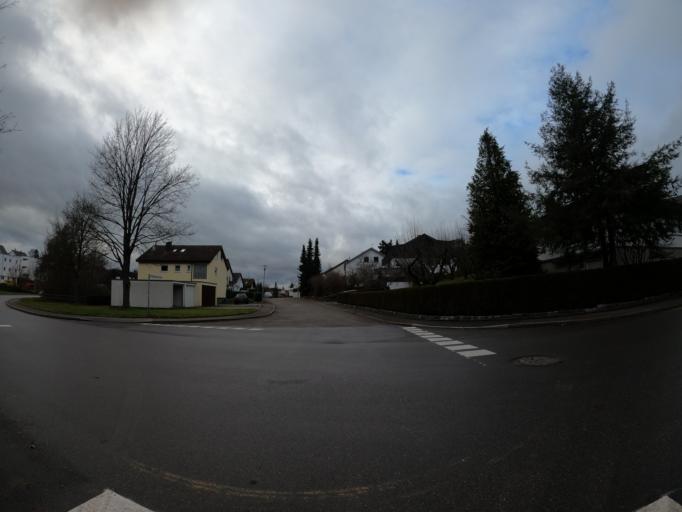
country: DE
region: Baden-Wuerttemberg
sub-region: Regierungsbezirk Stuttgart
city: Waldstetten
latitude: 48.7665
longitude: 9.8324
